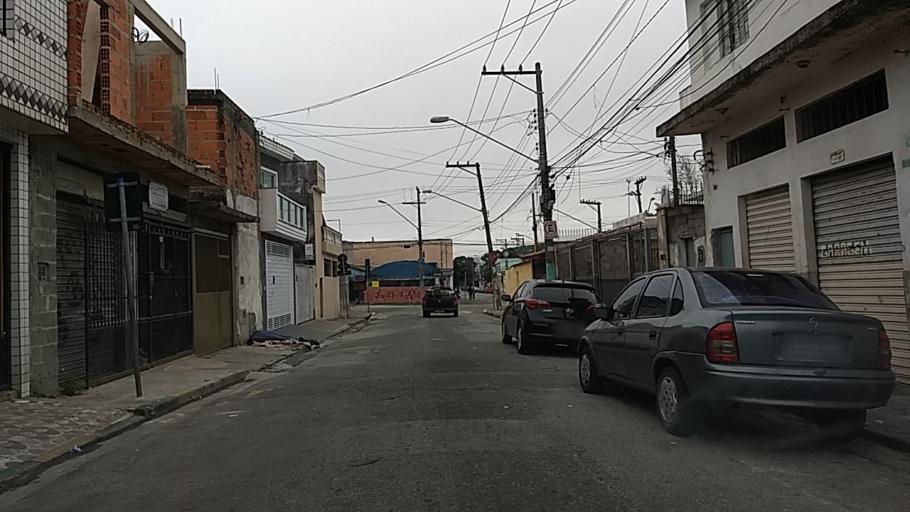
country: BR
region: Sao Paulo
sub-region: Guarulhos
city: Guarulhos
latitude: -23.4945
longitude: -46.5764
